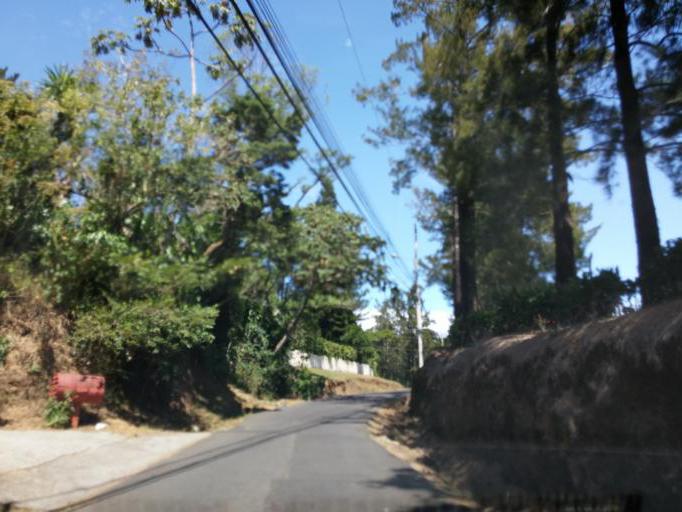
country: CR
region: Heredia
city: Santo Domingo
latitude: 10.0608
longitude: -84.1339
